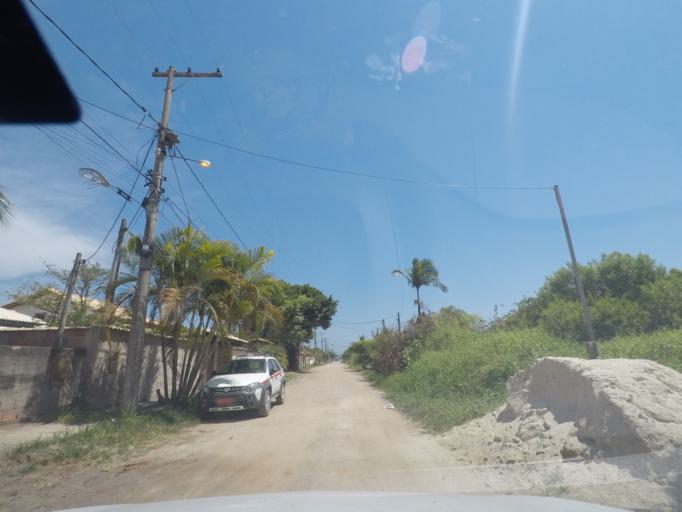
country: BR
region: Rio de Janeiro
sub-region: Marica
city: Marica
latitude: -22.9547
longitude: -42.9558
